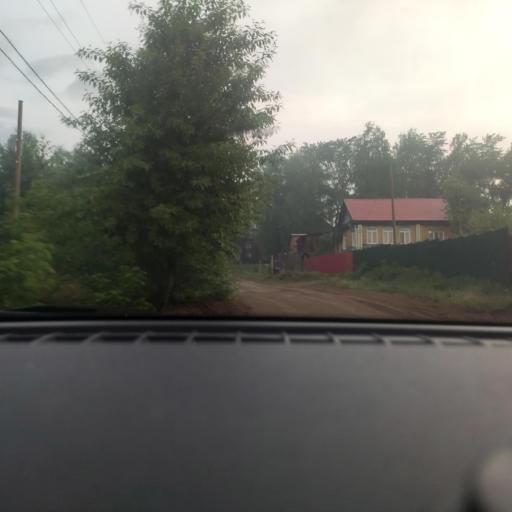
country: RU
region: Perm
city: Nytva
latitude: 57.8917
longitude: 55.4868
